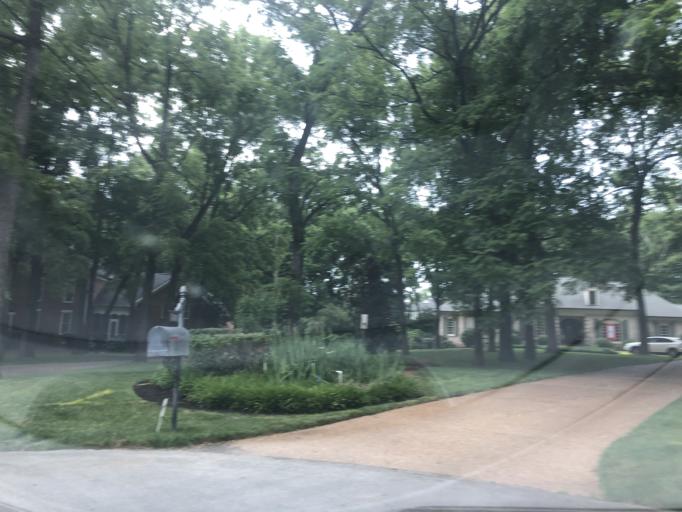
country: US
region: Tennessee
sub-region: Davidson County
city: Oak Hill
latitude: 36.0889
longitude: -86.7791
